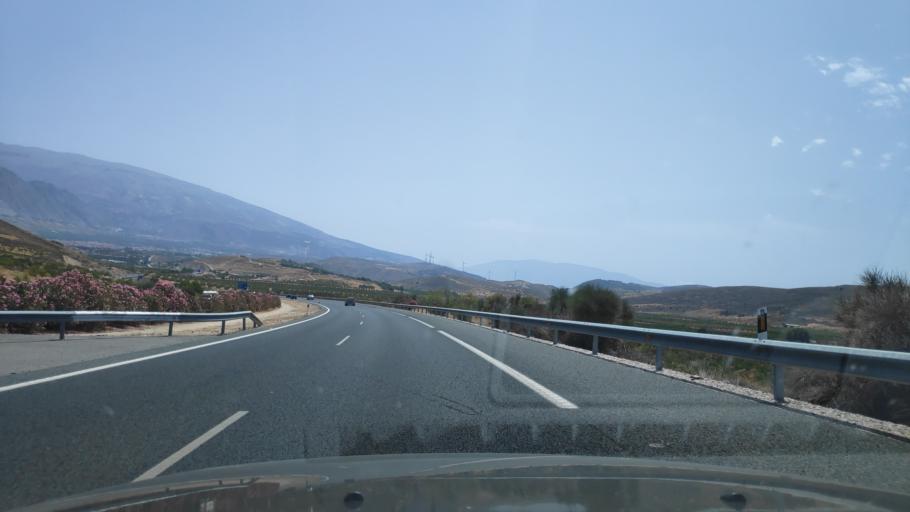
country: ES
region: Andalusia
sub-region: Provincia de Granada
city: Padul
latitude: 36.9921
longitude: -3.6255
